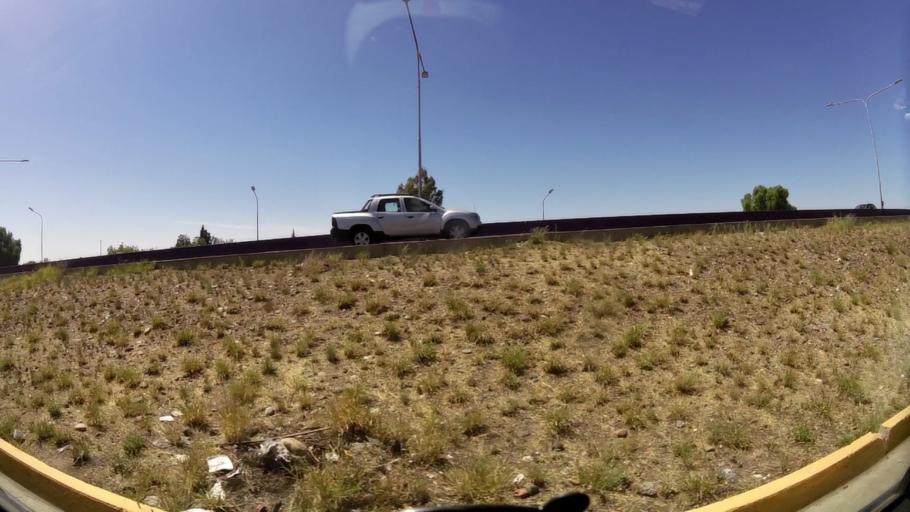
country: AR
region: Mendoza
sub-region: Departamento de Godoy Cruz
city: Godoy Cruz
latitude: -32.9314
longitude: -68.8641
